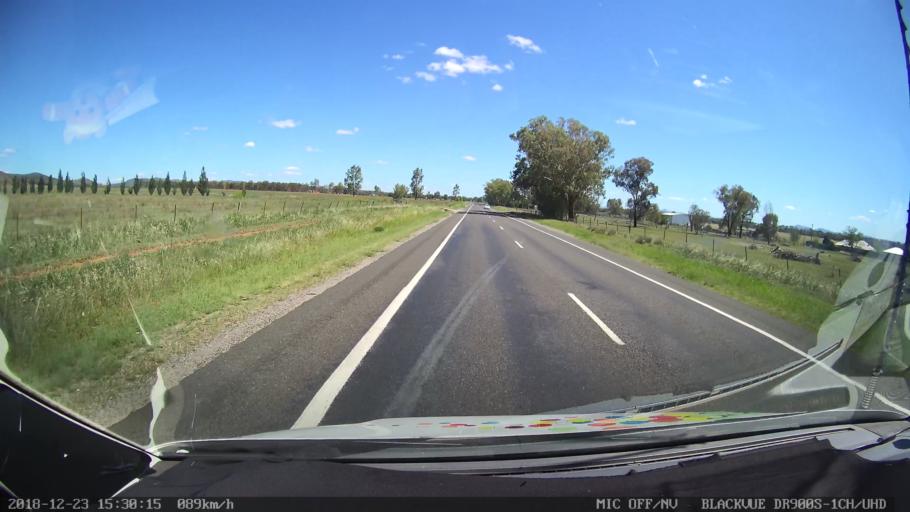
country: AU
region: New South Wales
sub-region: Tamworth Municipality
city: East Tamworth
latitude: -30.9562
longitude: 150.8663
